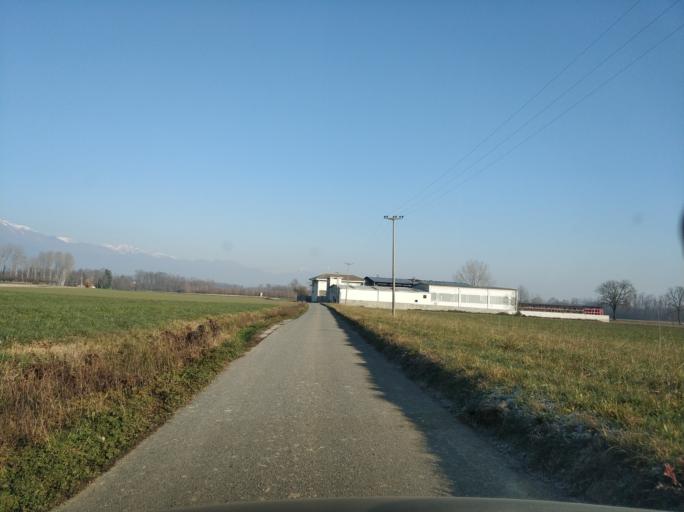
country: IT
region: Piedmont
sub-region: Provincia di Torino
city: Barbania
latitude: 45.3046
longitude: 7.6418
